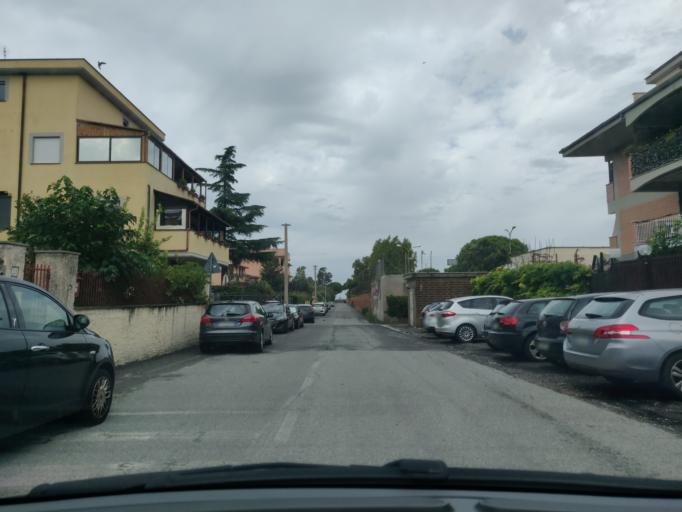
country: IT
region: Latium
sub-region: Citta metropolitana di Roma Capitale
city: Aurelia
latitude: 42.1381
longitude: 11.7884
